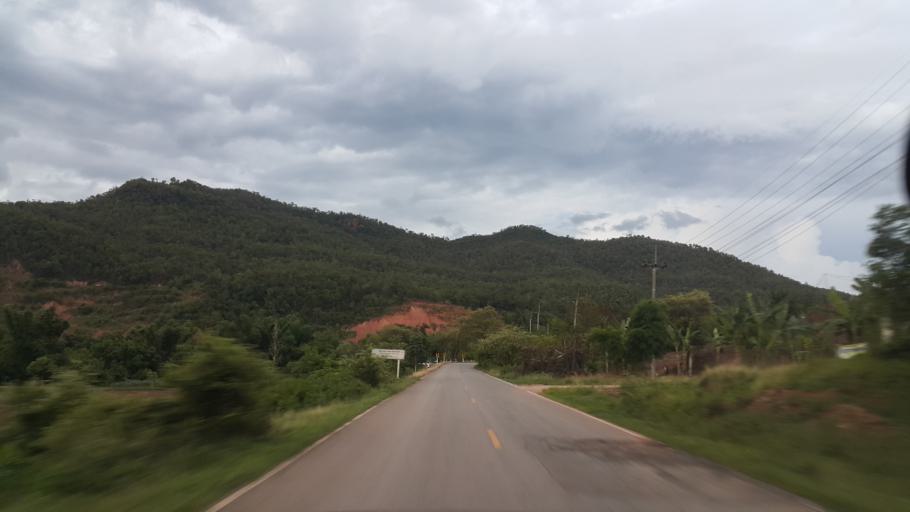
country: TH
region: Loei
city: Na Haeo
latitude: 17.5271
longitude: 101.1848
